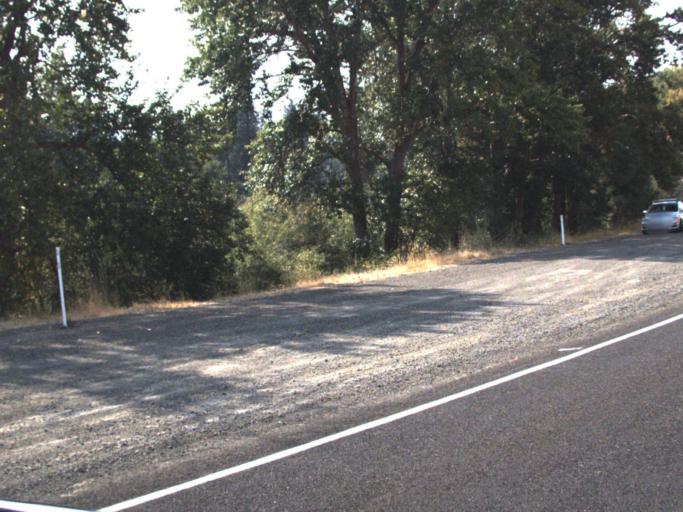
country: US
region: Washington
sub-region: Kittitas County
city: Ellensburg
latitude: 47.0996
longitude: -120.6925
